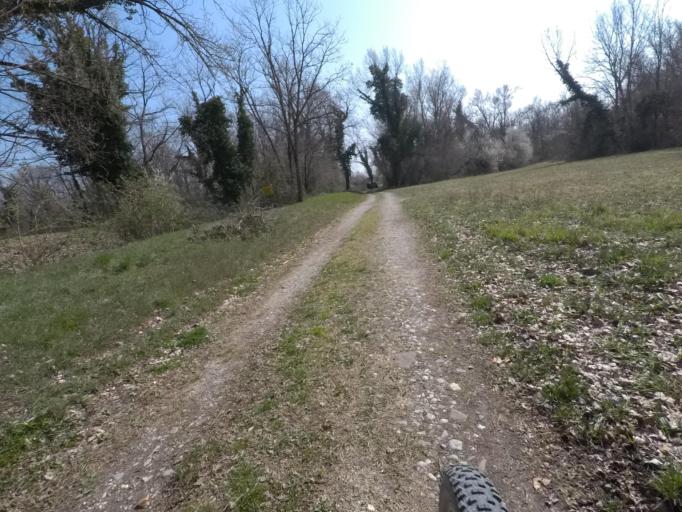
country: IT
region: Friuli Venezia Giulia
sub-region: Provincia di Udine
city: Remanzacco
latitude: 46.0592
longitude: 13.3250
